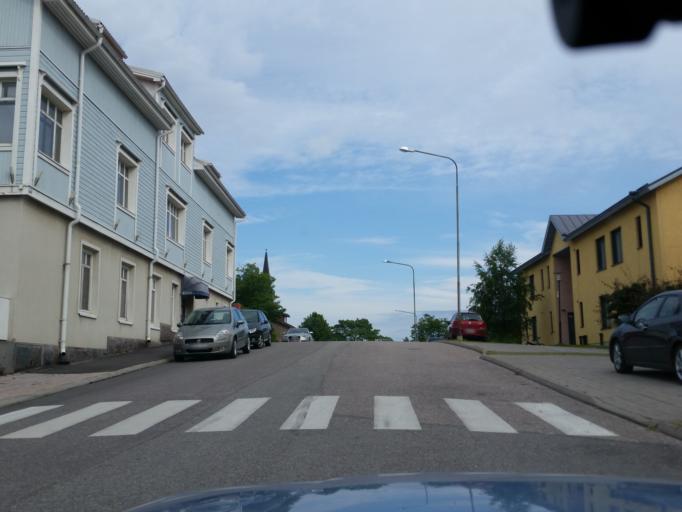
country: FI
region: Uusimaa
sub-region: Raaseporin
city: Hanko
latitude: 59.8247
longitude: 22.9656
